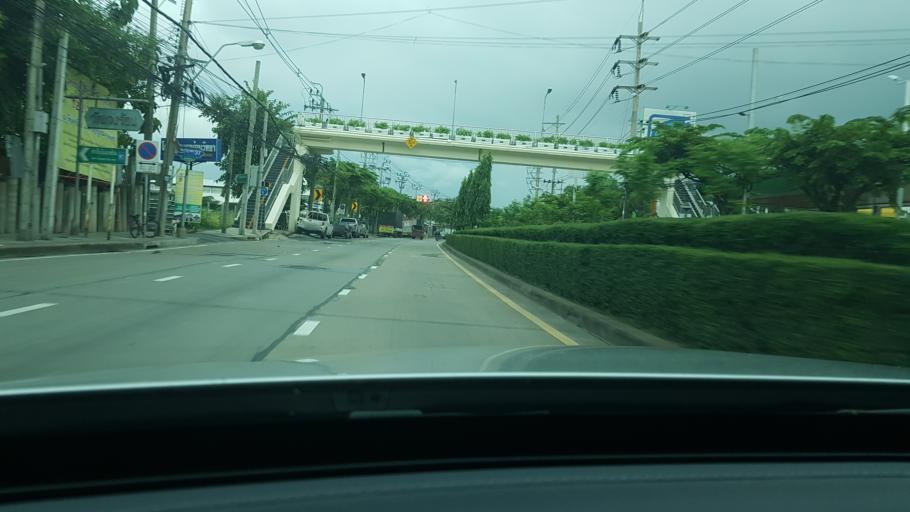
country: TH
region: Bangkok
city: Rat Burana
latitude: 13.6737
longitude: 100.5181
